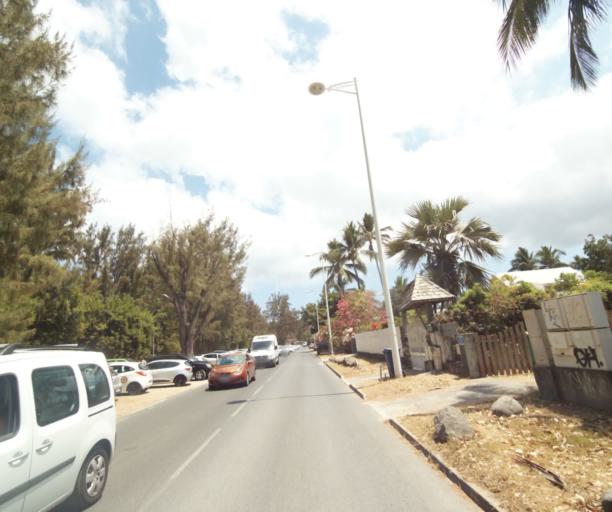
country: RE
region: Reunion
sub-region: Reunion
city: Trois-Bassins
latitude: -21.0806
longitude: 55.2242
